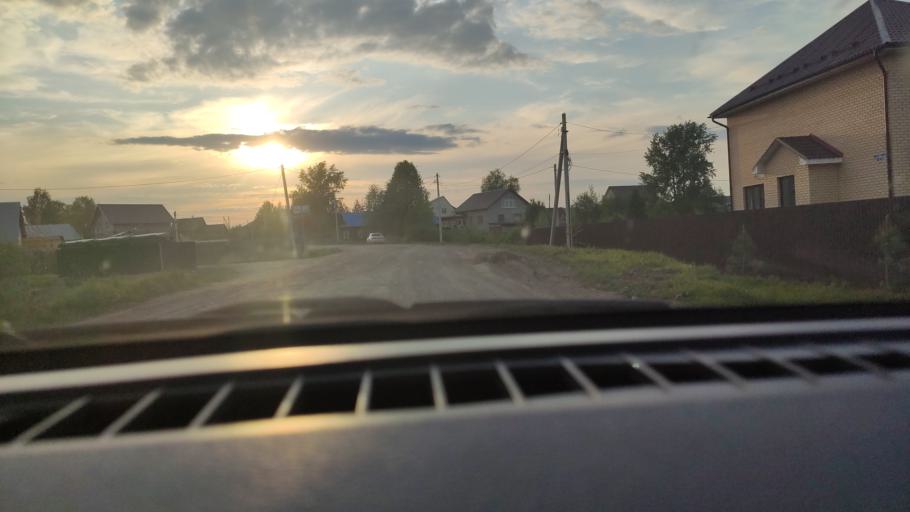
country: RU
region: Perm
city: Overyata
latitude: 58.0784
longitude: 55.9768
